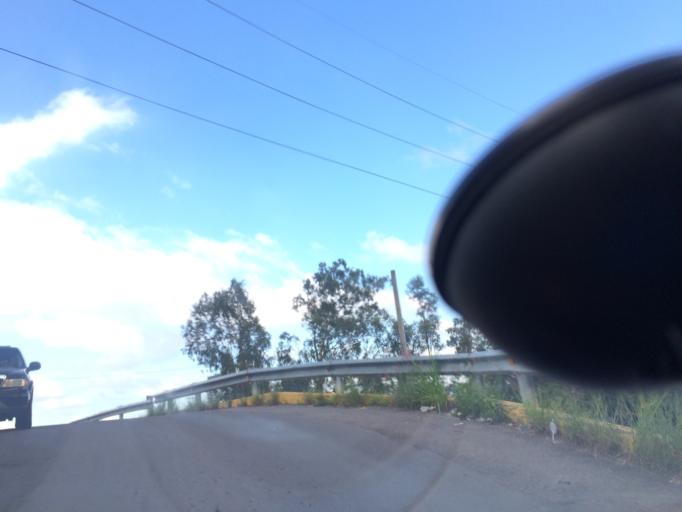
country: MX
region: Nayarit
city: Tepic
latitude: 21.4999
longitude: -104.9118
